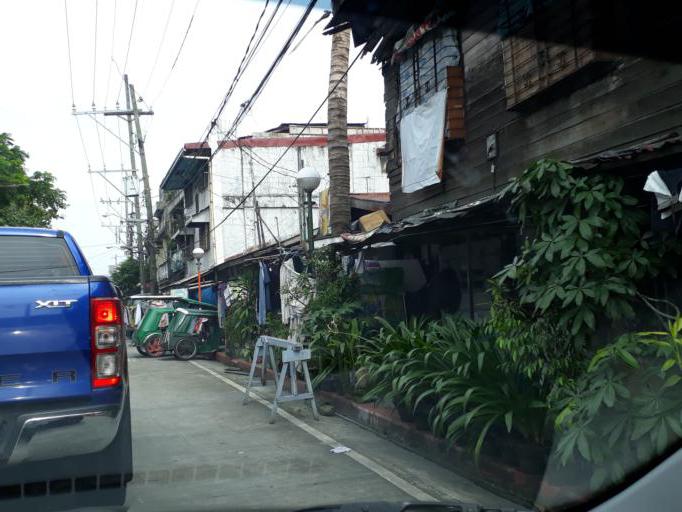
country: PH
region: Metro Manila
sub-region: City of Manila
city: Manila
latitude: 14.6223
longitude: 120.9841
